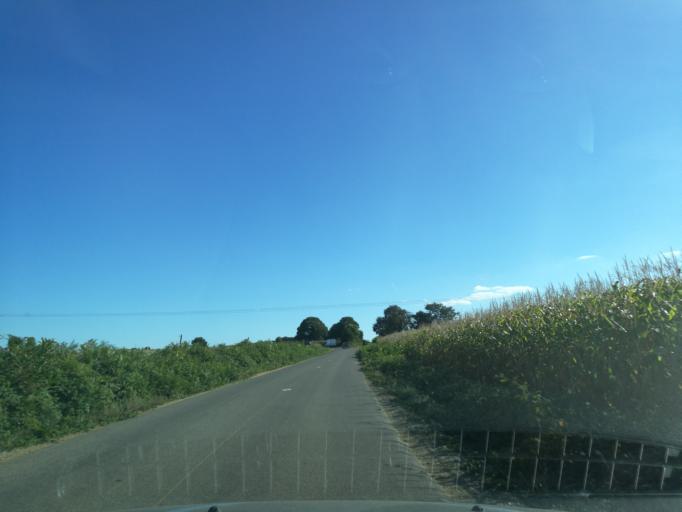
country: FR
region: Brittany
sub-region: Departement d'Ille-et-Vilaine
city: Montauban-de-Bretagne
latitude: 48.1777
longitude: -2.0398
